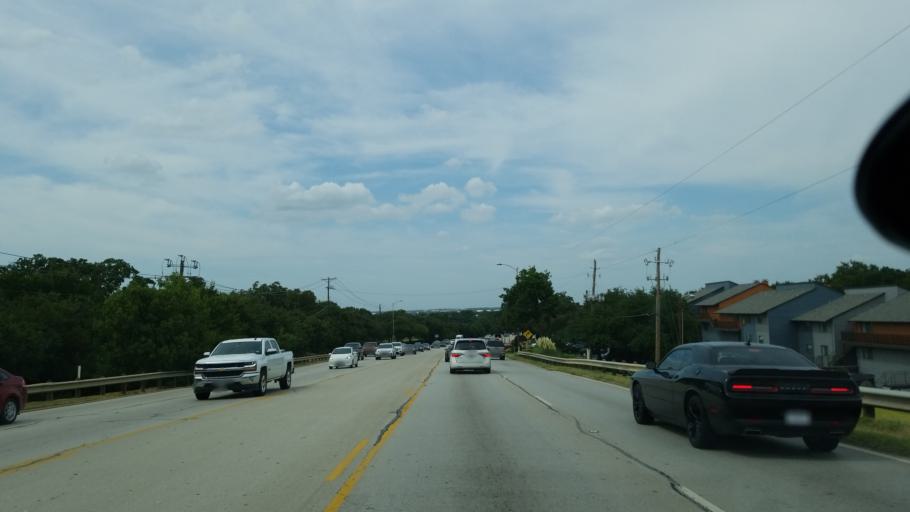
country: US
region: Texas
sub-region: Tarrant County
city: Arlington
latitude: 32.7761
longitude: -97.0971
